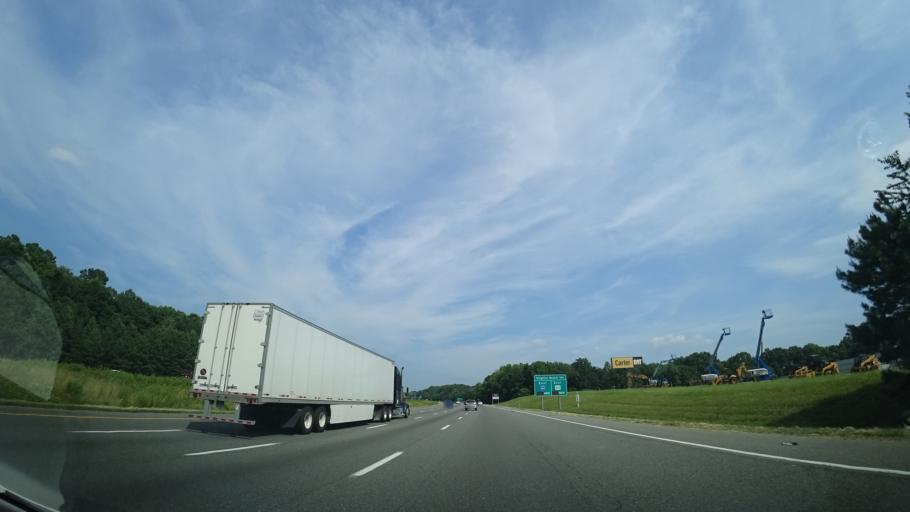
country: US
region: Virginia
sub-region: Henrico County
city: Chamberlayne
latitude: 37.6389
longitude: -77.4068
